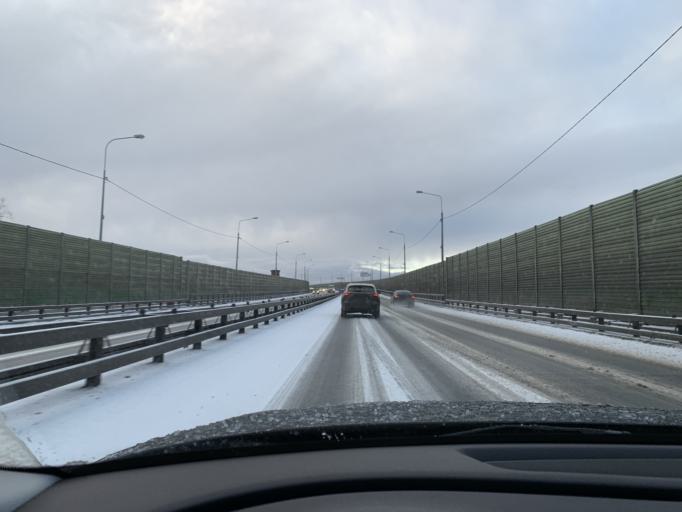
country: RU
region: Moskovskaya
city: Sheremet'yevskiy
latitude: 55.9746
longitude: 37.5104
